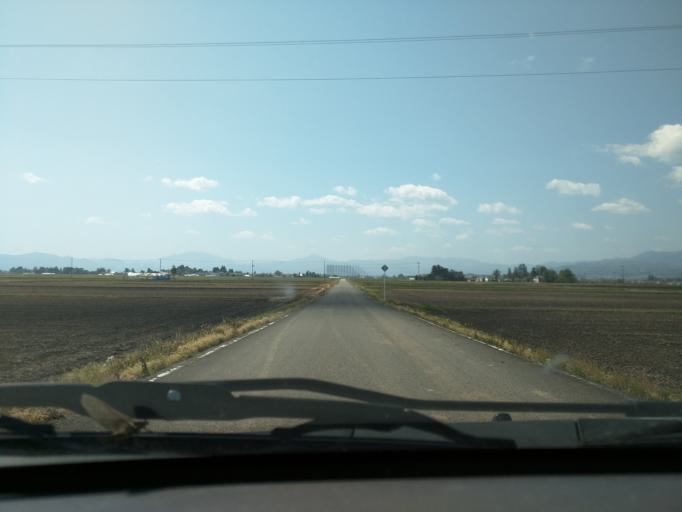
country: JP
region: Fukushima
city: Kitakata
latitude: 37.5761
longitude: 139.8353
